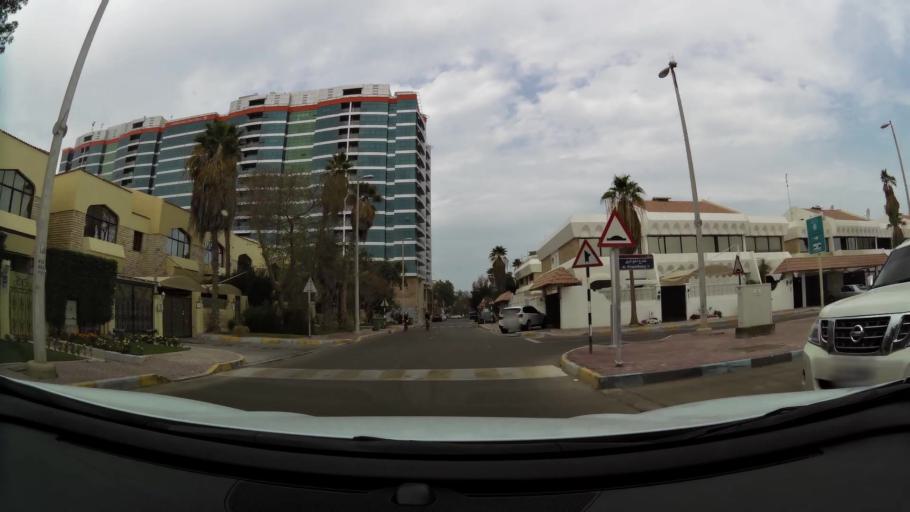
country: AE
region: Abu Dhabi
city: Abu Dhabi
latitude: 24.4670
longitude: 54.3357
